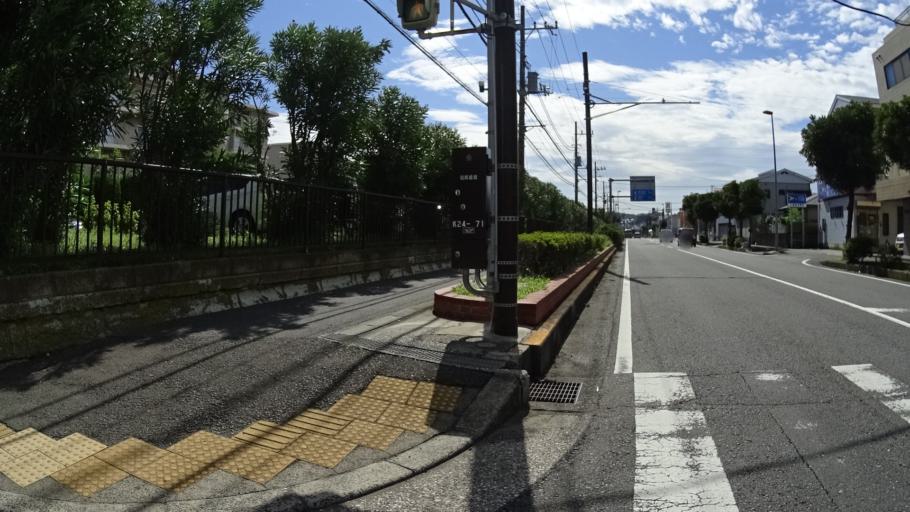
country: JP
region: Kanagawa
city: Yokosuka
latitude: 35.2626
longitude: 139.6959
